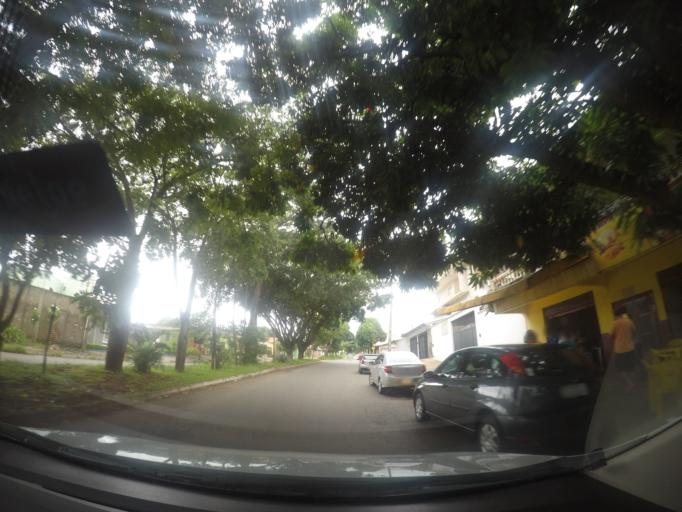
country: BR
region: Goias
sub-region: Goiania
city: Goiania
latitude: -16.6158
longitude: -49.2984
